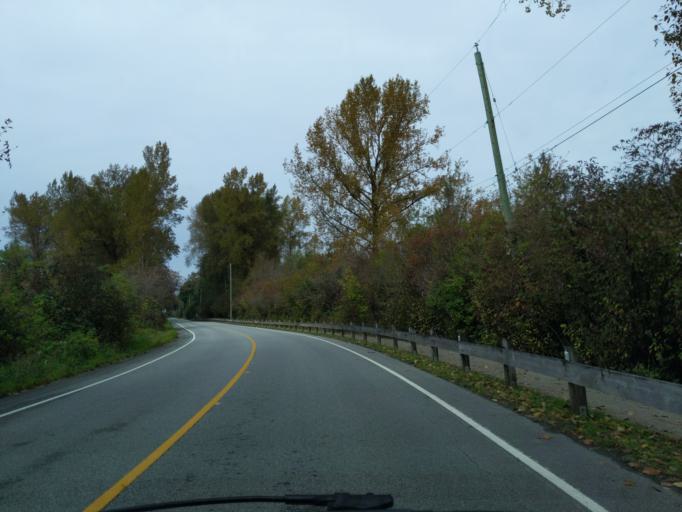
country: CA
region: British Columbia
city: Maple Ridge
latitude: 49.2004
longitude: -122.5950
